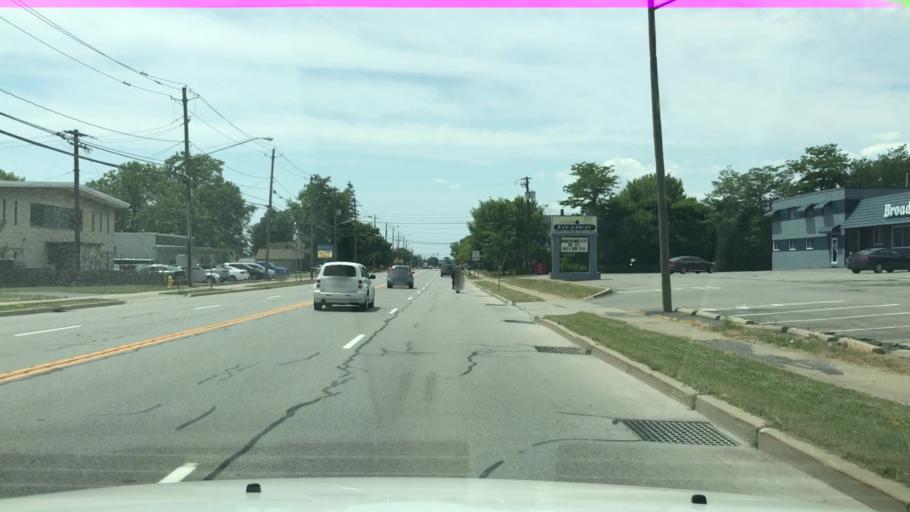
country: US
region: New York
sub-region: Erie County
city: Cheektowaga
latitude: 42.9039
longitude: -78.7456
